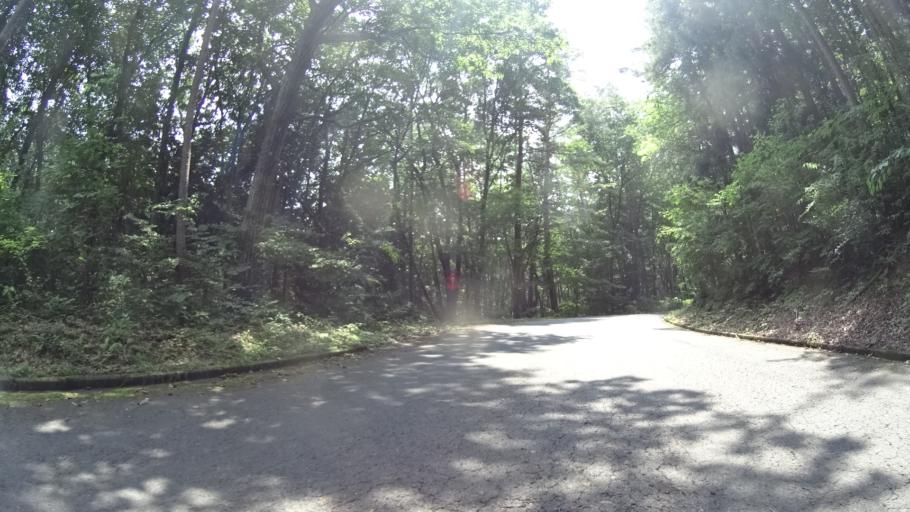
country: JP
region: Nagano
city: Saku
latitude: 36.0910
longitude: 138.6945
